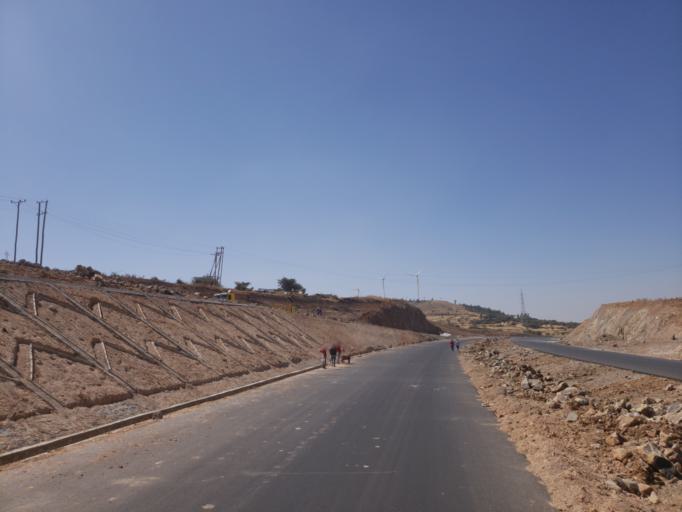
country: ET
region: Oromiya
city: Mojo
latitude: 8.5668
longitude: 39.1639
